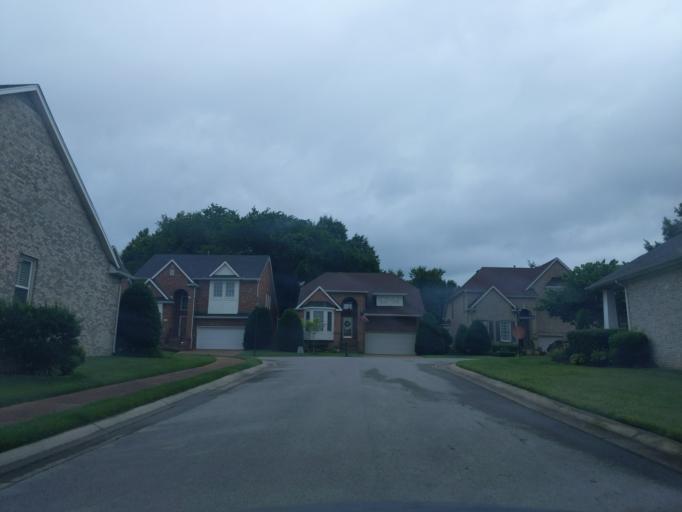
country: US
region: Tennessee
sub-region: Williamson County
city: Brentwood
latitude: 36.0405
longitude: -86.7588
